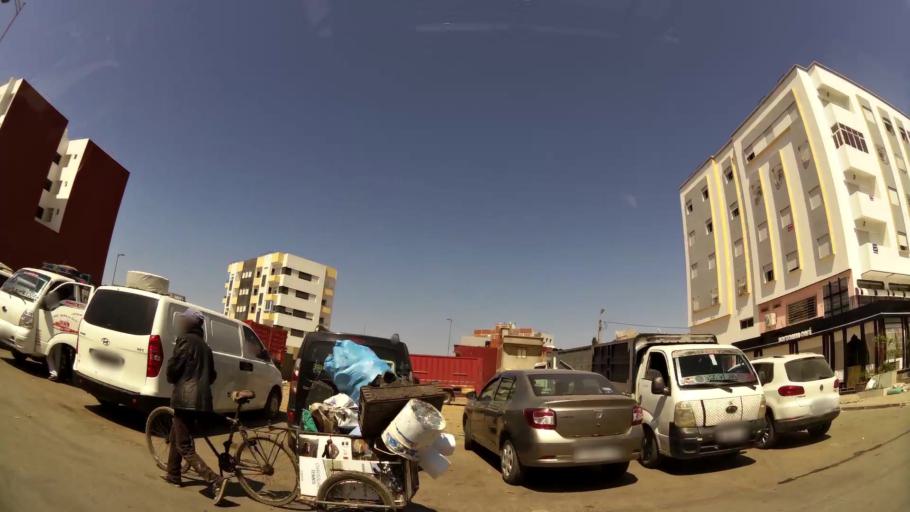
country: MA
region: Gharb-Chrarda-Beni Hssen
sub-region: Kenitra Province
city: Kenitra
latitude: 34.2439
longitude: -6.5508
